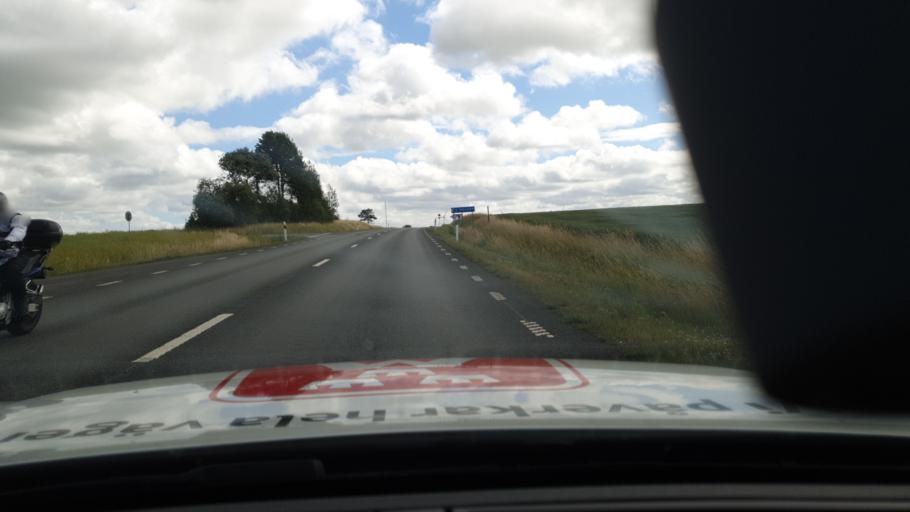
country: SE
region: Vaestra Goetaland
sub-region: Falkopings Kommun
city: Akarp
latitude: 58.1257
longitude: 13.6900
